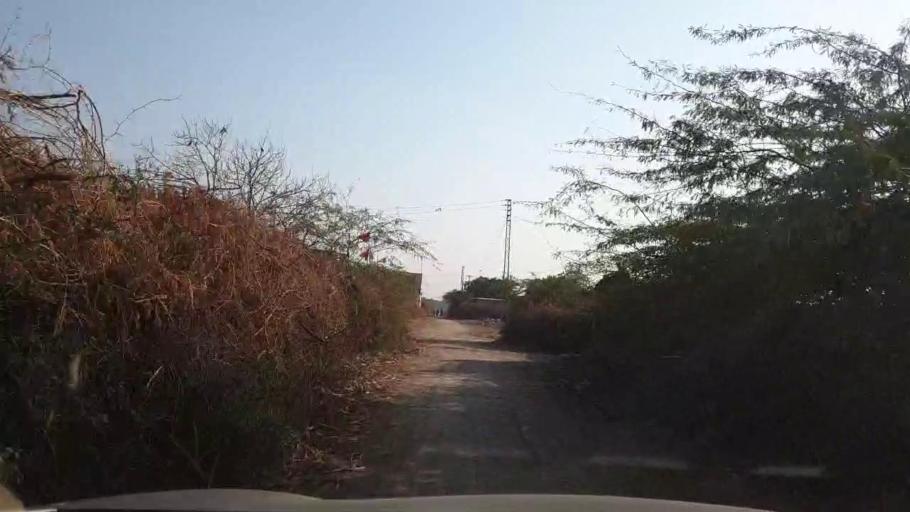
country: PK
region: Sindh
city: Tando Allahyar
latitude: 25.5047
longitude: 68.8500
